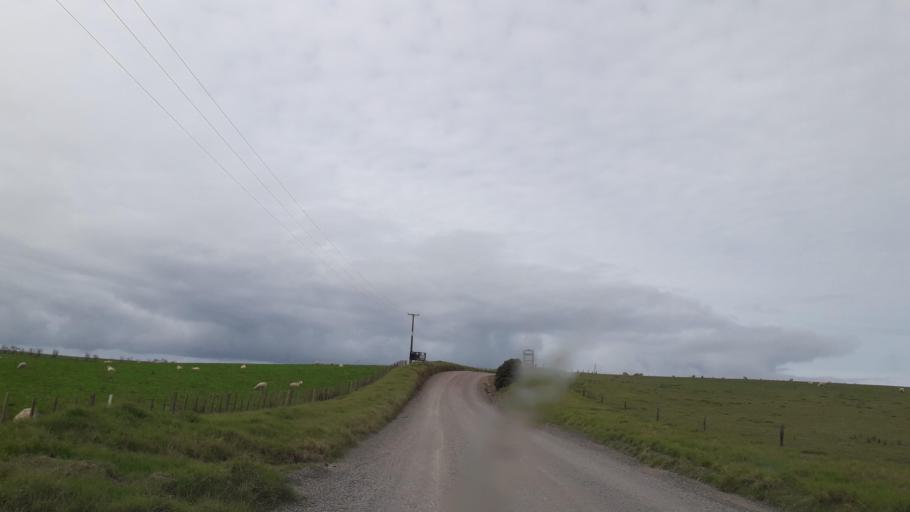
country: NZ
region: Northland
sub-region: Far North District
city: Kerikeri
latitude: -35.1311
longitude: 174.0034
